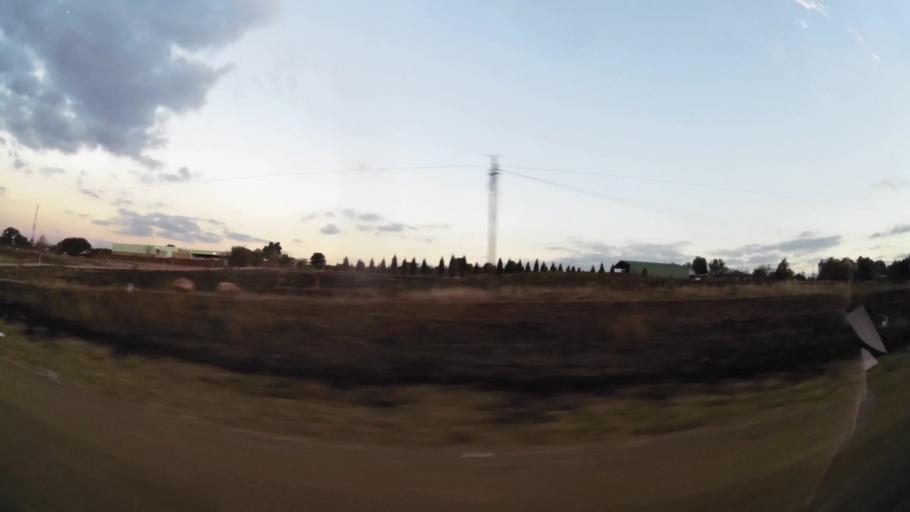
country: ZA
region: Gauteng
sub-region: West Rand District Municipality
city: Krugersdorp
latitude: -26.0690
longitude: 27.6835
